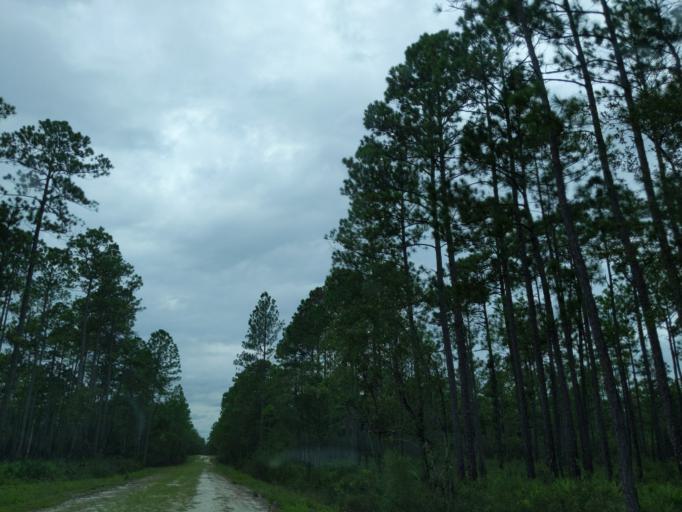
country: US
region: Florida
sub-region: Gadsden County
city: Midway
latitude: 30.3542
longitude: -84.5032
